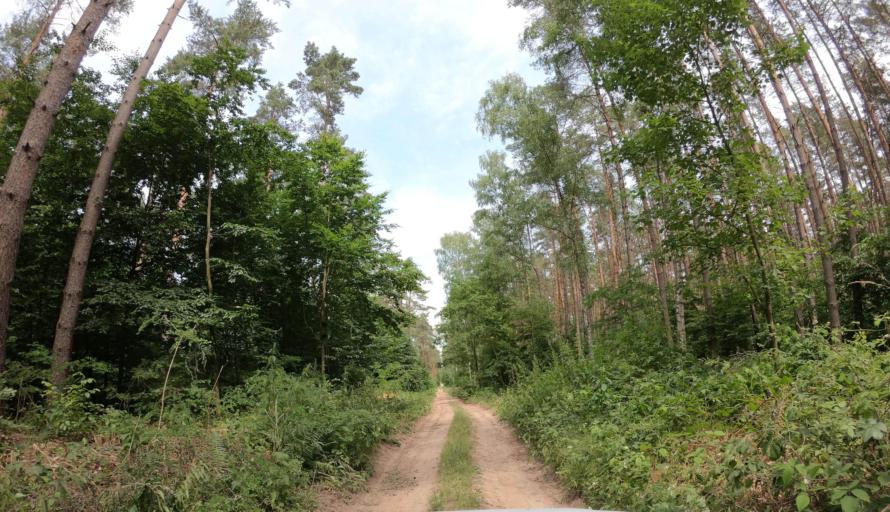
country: PL
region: West Pomeranian Voivodeship
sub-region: Powiat pyrzycki
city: Kozielice
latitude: 53.0222
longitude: 14.7470
